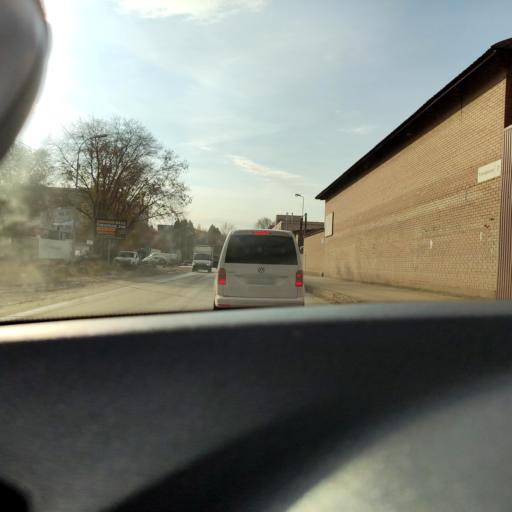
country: RU
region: Samara
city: Petra-Dubrava
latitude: 53.2361
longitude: 50.2943
